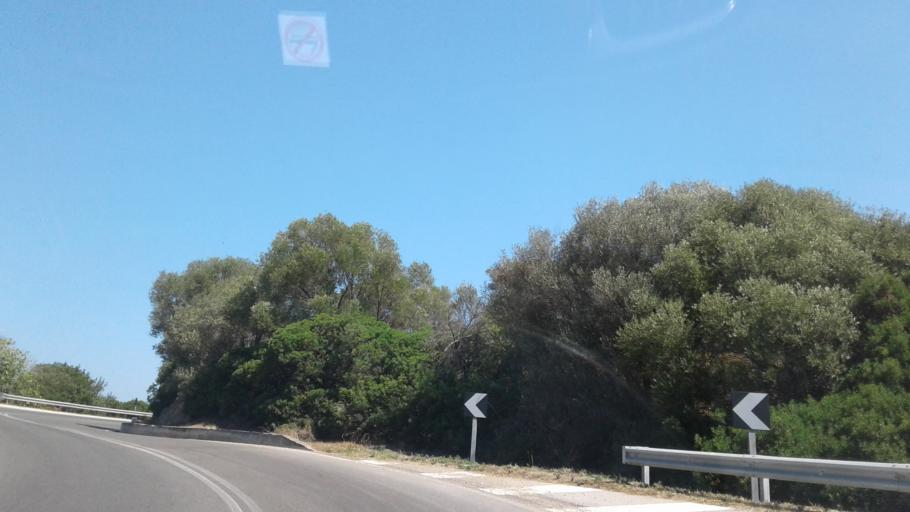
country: IT
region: Sardinia
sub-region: Provincia di Olbia-Tempio
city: Palau
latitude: 41.1690
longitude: 9.3181
